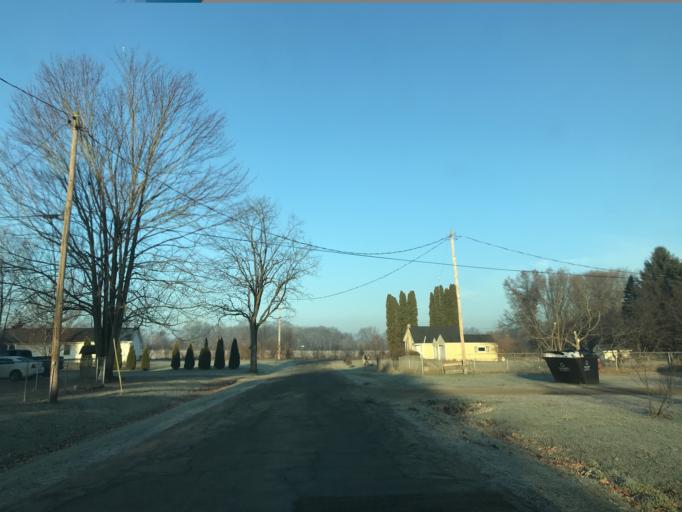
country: US
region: Michigan
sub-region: Eaton County
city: Eaton Rapids
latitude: 42.4454
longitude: -84.5659
